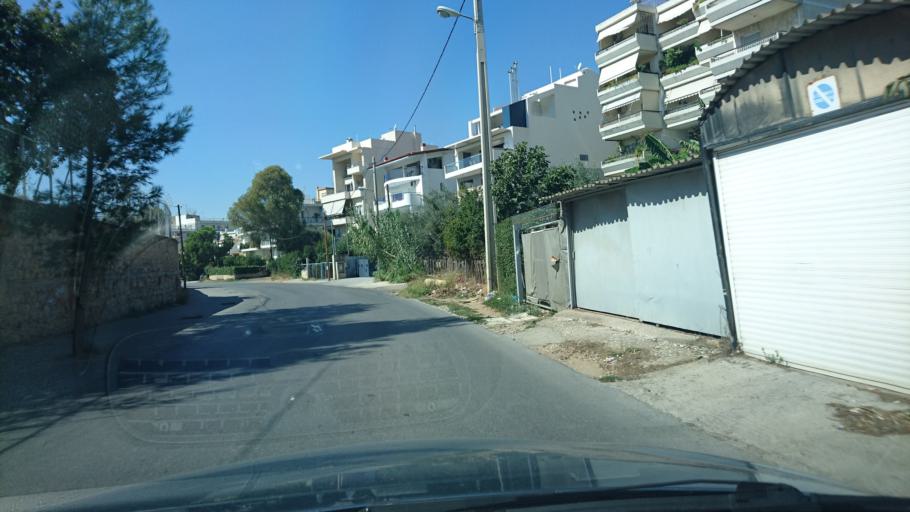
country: GR
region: Attica
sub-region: Nomarchia Athinas
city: Khalandrion
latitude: 38.0136
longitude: 23.8045
